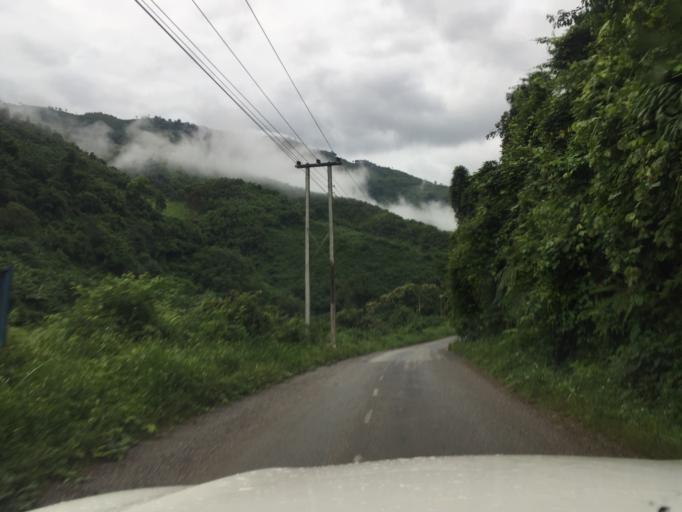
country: LA
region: Oudomxai
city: Muang La
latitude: 21.0088
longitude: 102.2336
